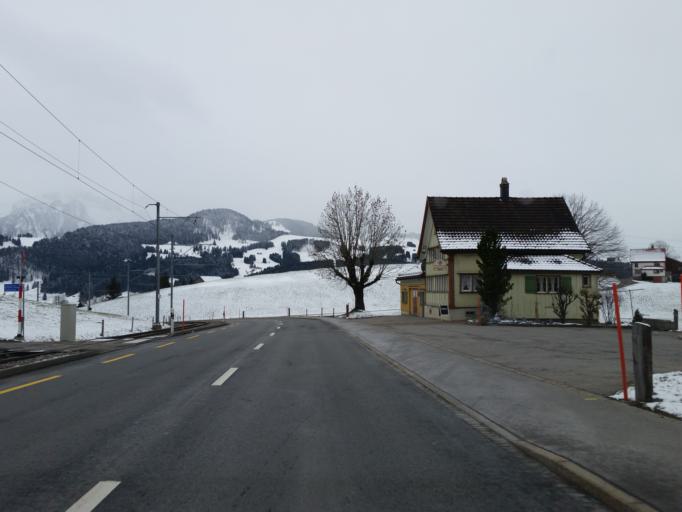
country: CH
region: Appenzell Innerrhoden
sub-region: Appenzell Inner Rhodes
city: Appenzell
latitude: 47.3415
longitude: 9.4288
